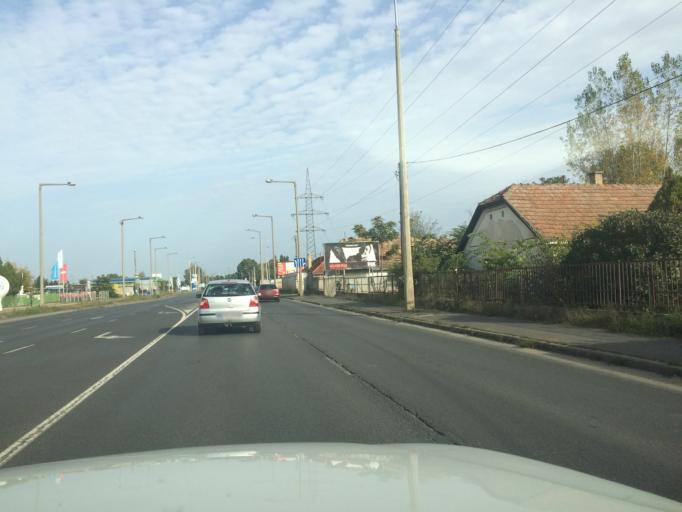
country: HU
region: Szabolcs-Szatmar-Bereg
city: Nyiregyhaza
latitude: 47.9339
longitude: 21.7188
